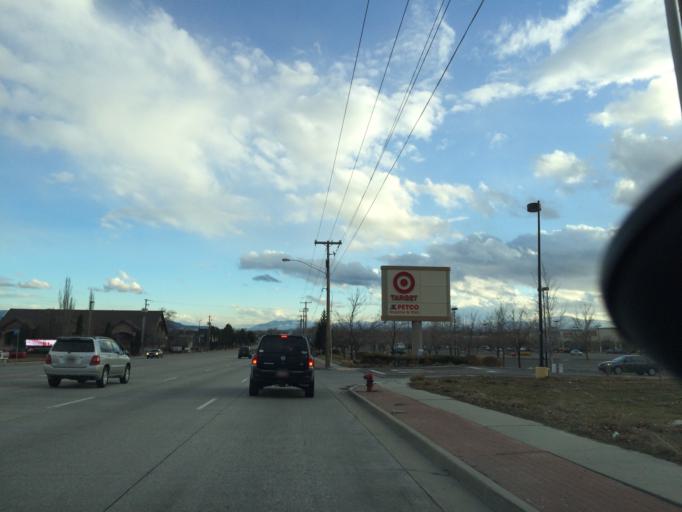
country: US
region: Utah
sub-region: Salt Lake County
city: West Jordan
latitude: 40.6297
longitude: -111.9389
